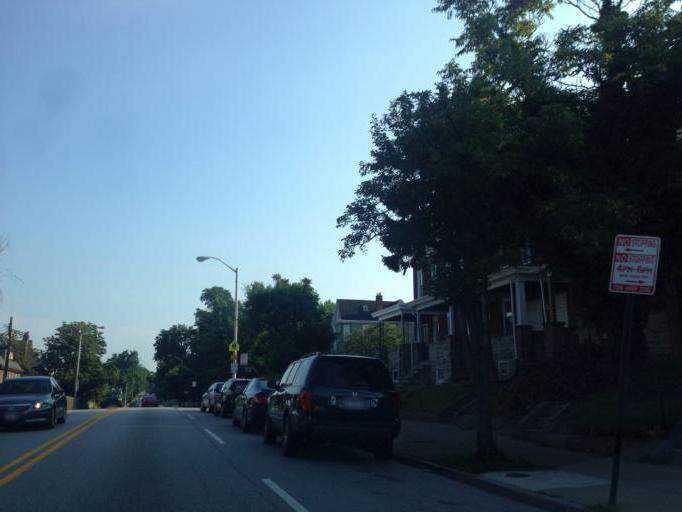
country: US
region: Maryland
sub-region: City of Baltimore
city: Baltimore
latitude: 39.3325
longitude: -76.6095
